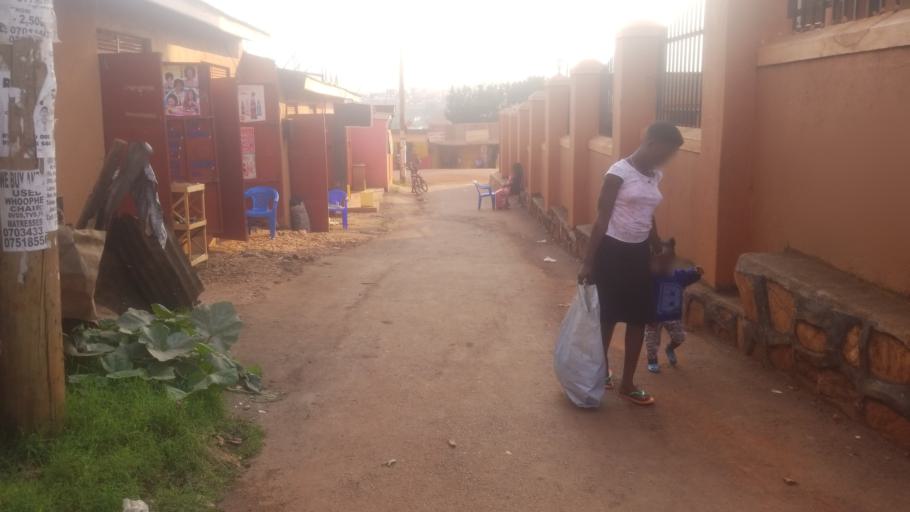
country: UG
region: Central Region
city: Kampala Central Division
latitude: 0.3374
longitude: 32.5618
